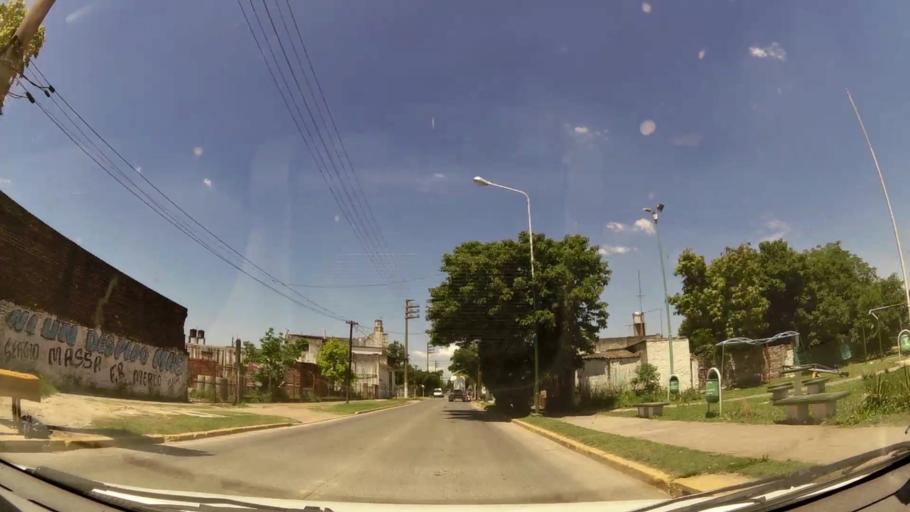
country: AR
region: Buenos Aires
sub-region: Partido de Merlo
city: Merlo
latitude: -34.6486
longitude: -58.7211
